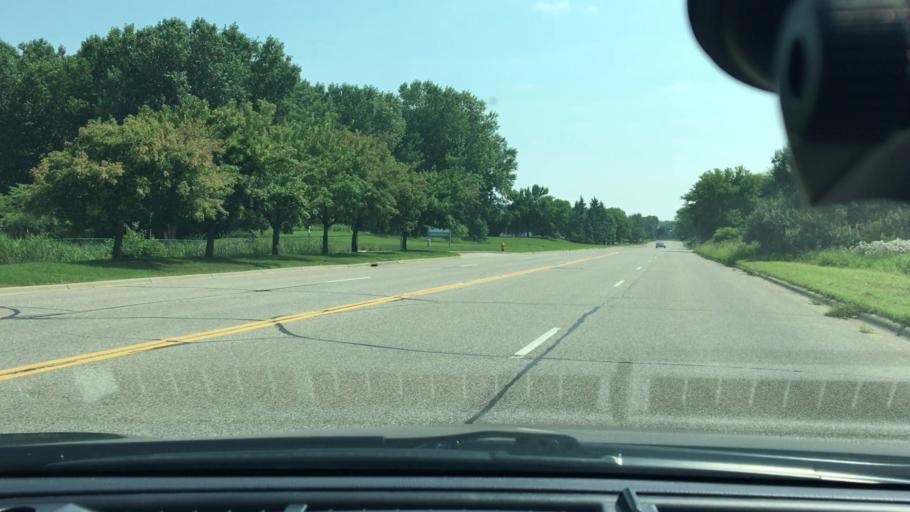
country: US
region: Minnesota
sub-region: Hennepin County
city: Plymouth
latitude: 44.9895
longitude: -93.4116
